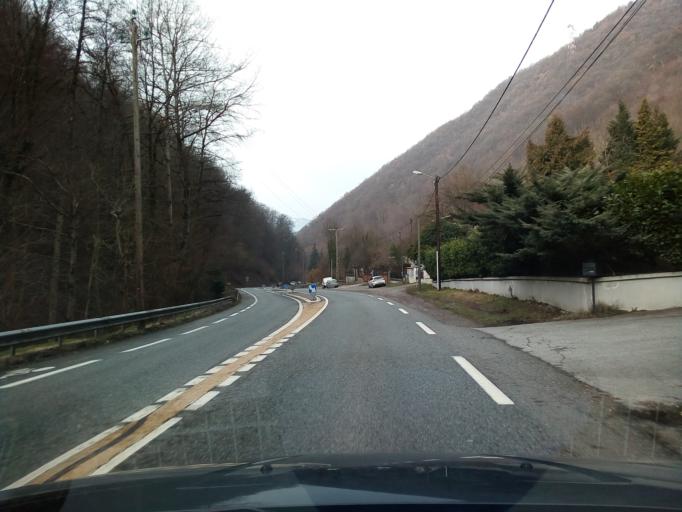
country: FR
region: Rhone-Alpes
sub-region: Departement de l'Isere
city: Gieres
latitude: 45.1628
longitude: 5.8139
